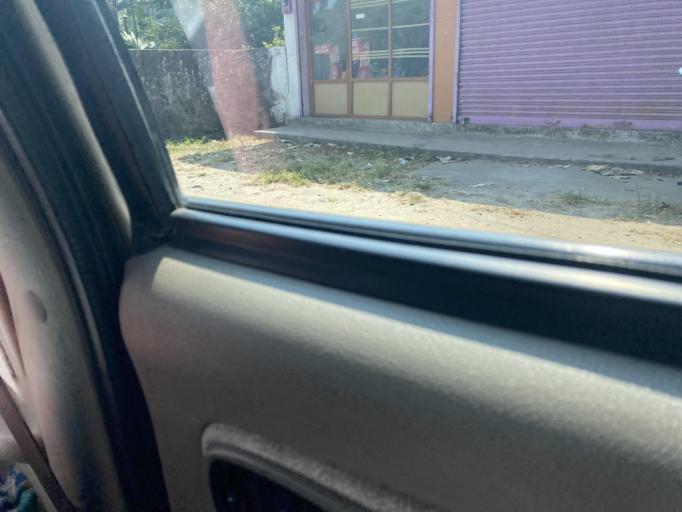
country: IN
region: Kerala
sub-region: Ernakulam
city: Elur
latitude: 10.1102
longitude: 76.2293
